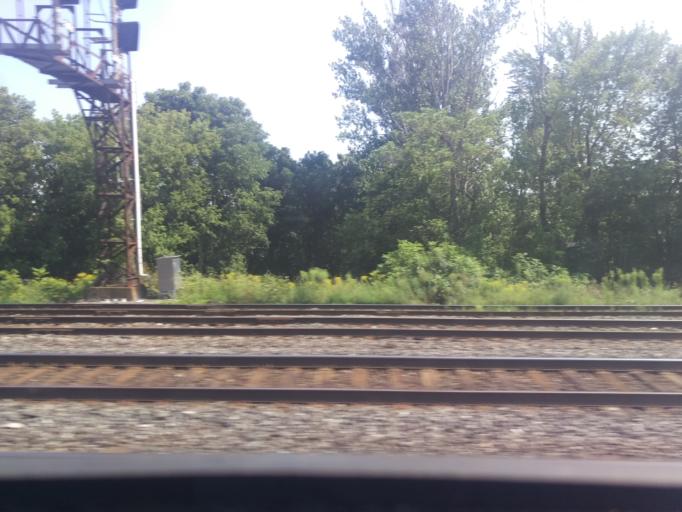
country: CA
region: Ontario
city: Brockville
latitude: 44.5892
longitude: -75.6978
